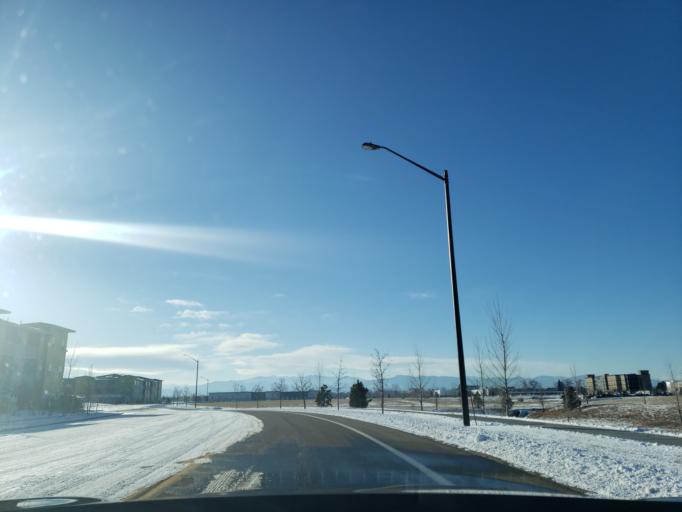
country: US
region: Colorado
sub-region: Larimer County
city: Fort Collins
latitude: 40.5197
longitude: -105.0077
